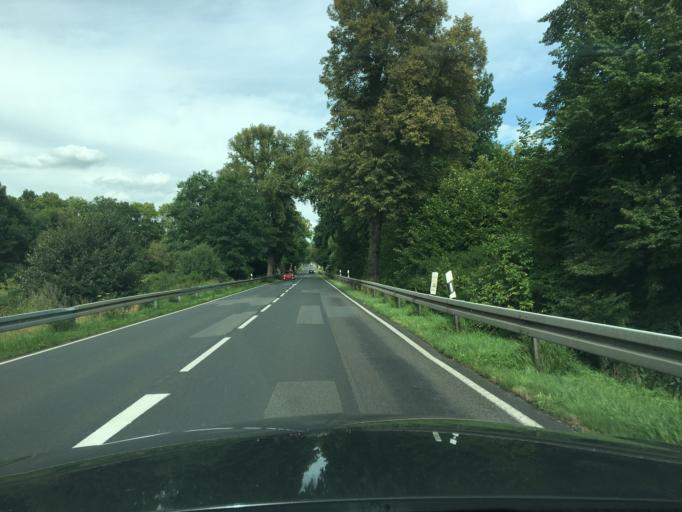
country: DE
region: Mecklenburg-Vorpommern
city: Wustrow
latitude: 53.4177
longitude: 13.1336
